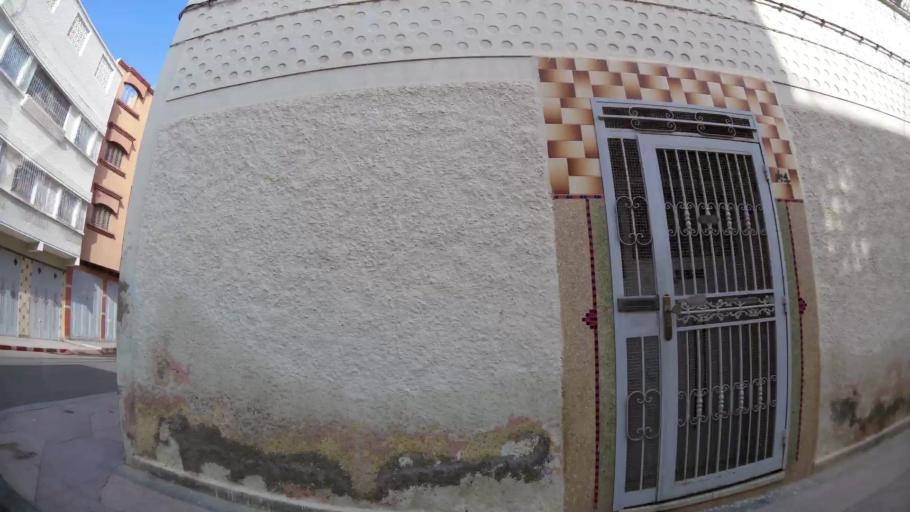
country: MA
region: Oriental
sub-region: Oujda-Angad
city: Oujda
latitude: 34.6944
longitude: -1.9035
